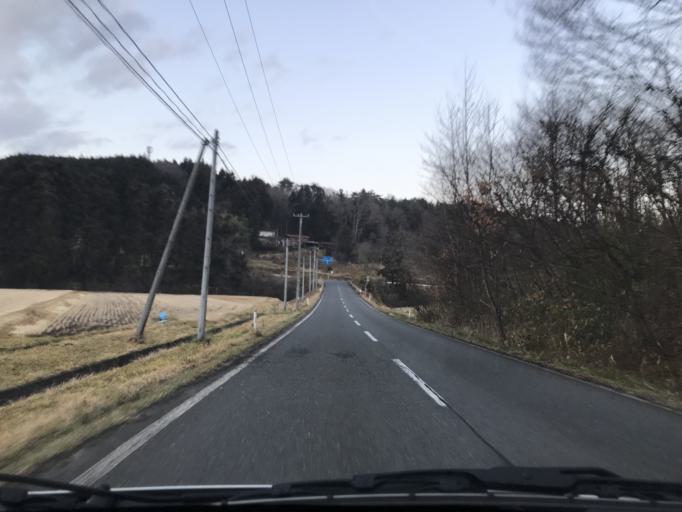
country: JP
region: Iwate
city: Ichinoseki
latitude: 38.8325
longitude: 141.1216
